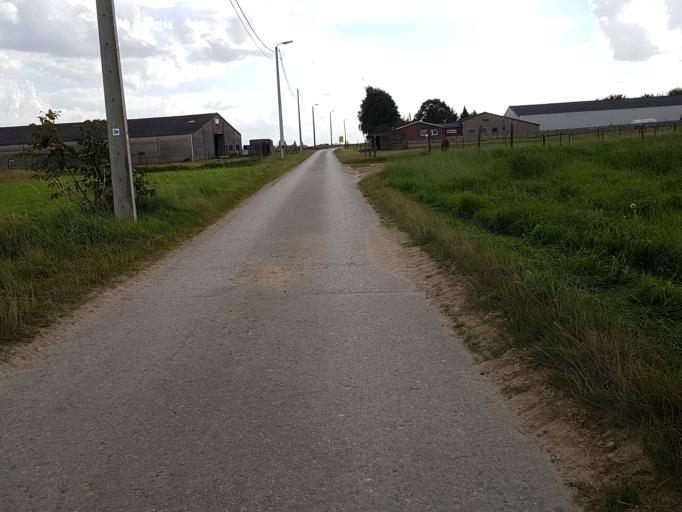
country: BE
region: Flanders
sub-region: Provincie Vlaams-Brabant
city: Kampenhout
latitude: 50.9183
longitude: 4.5574
